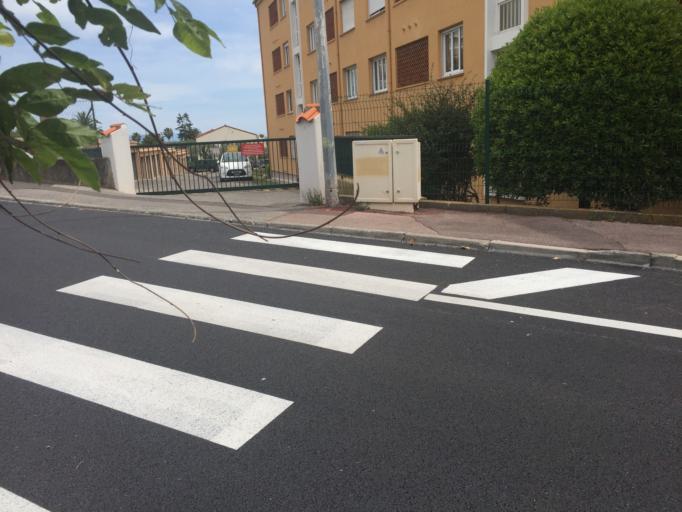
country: FR
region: Provence-Alpes-Cote d'Azur
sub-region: Departement des Alpes-Maritimes
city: Antibes
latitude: 43.5872
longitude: 7.1159
